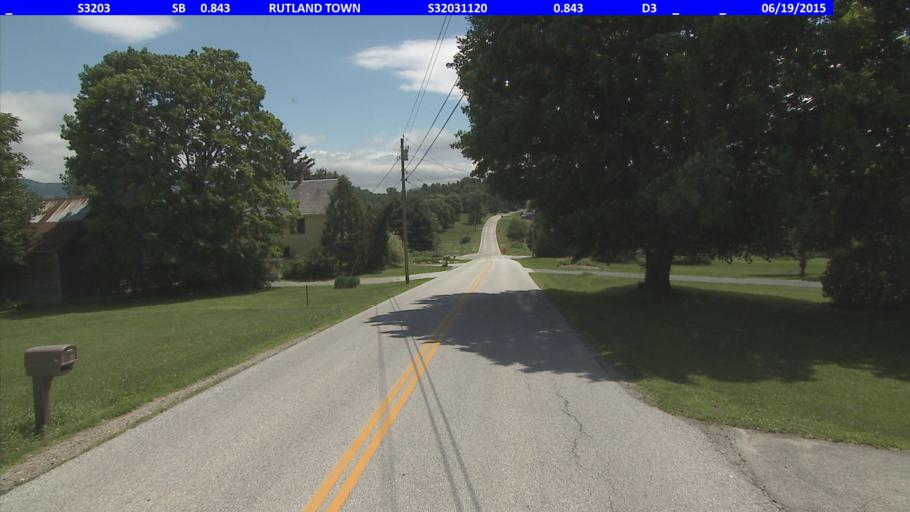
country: US
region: Vermont
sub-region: Rutland County
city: Rutland
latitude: 43.6648
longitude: -73.0015
